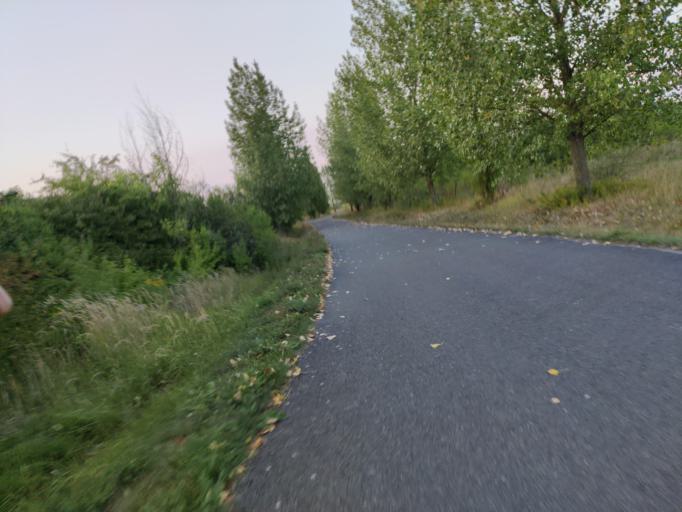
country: DE
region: Saxony
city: Zschortau
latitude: 51.4522
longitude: 12.3180
